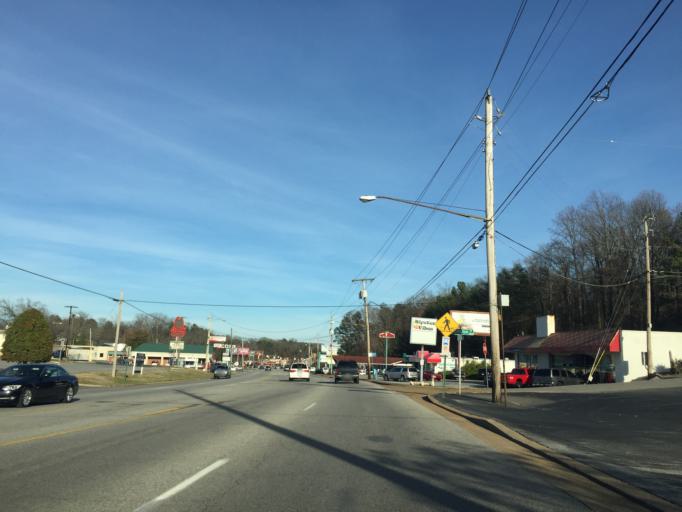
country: US
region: Tennessee
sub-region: Hamilton County
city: Red Bank
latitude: 35.1130
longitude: -85.2628
